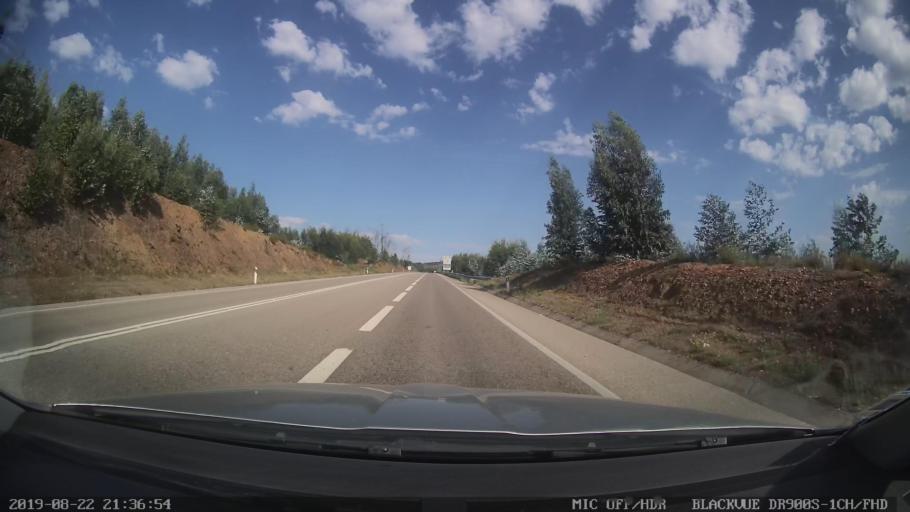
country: PT
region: Leiria
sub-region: Figueiro Dos Vinhos
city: Figueiro dos Vinhos
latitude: 39.9272
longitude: -8.2381
